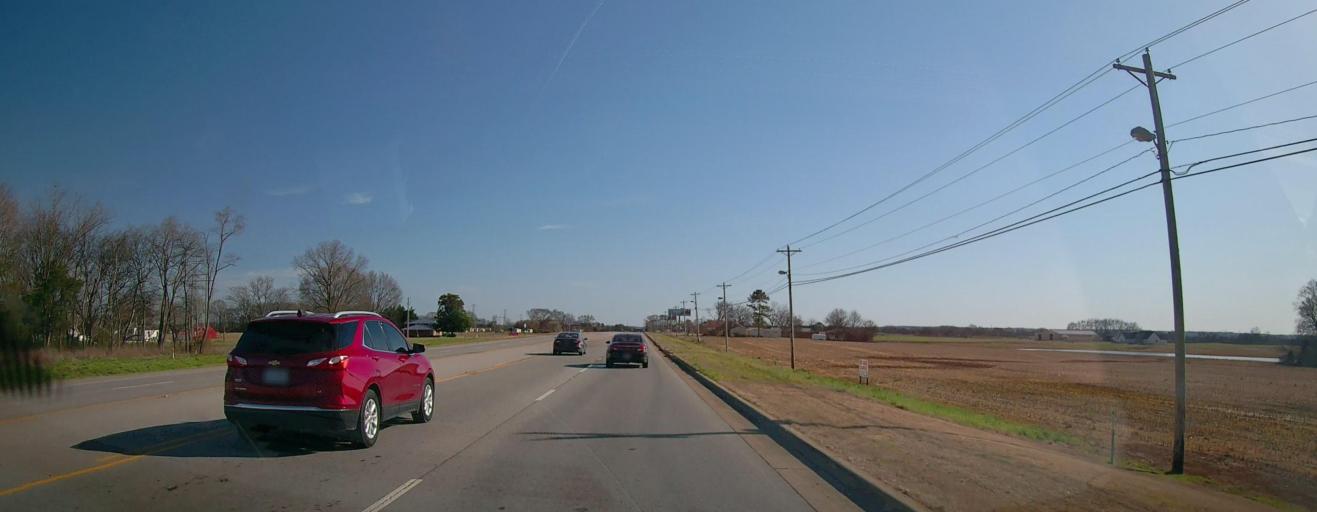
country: US
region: Alabama
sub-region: Colbert County
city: Muscle Shoals
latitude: 34.7270
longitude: -87.6352
